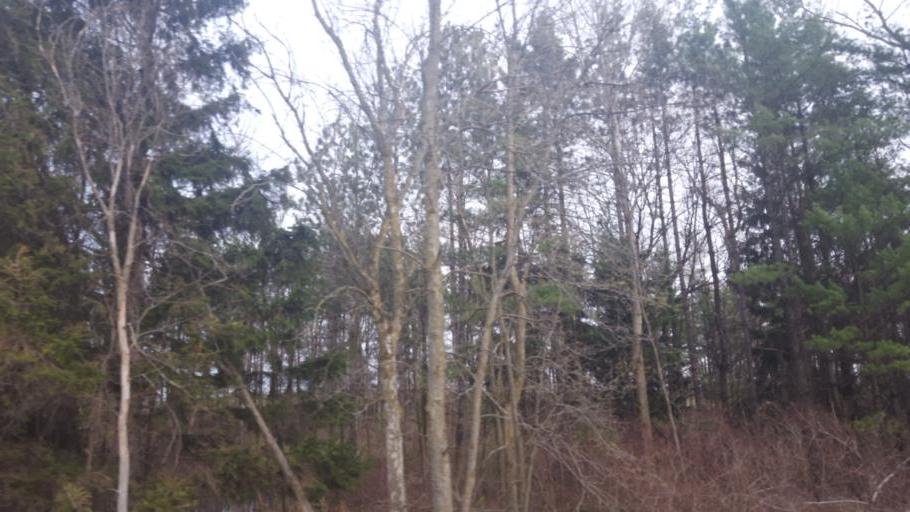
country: US
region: Michigan
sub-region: Midland County
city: Coleman
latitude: 43.8764
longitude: -84.6464
